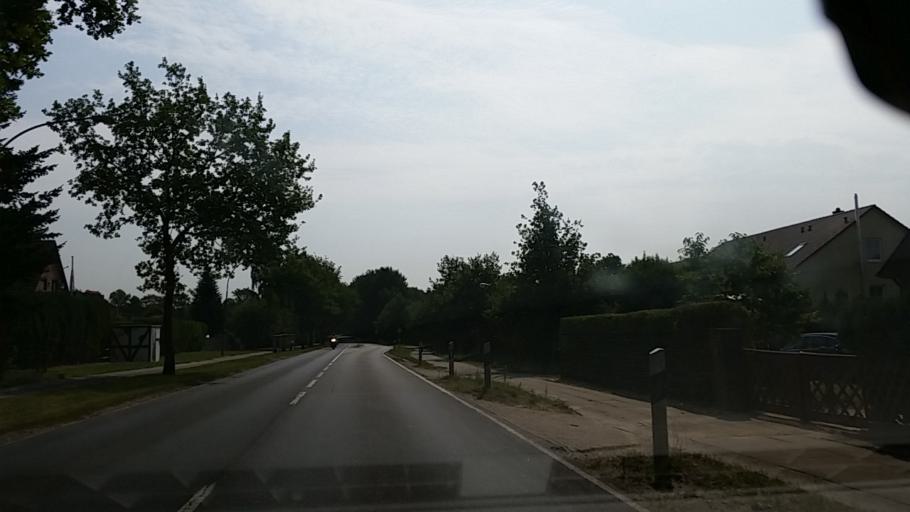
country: DE
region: Schleswig-Holstein
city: Glinde
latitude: 53.5414
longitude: 10.1888
